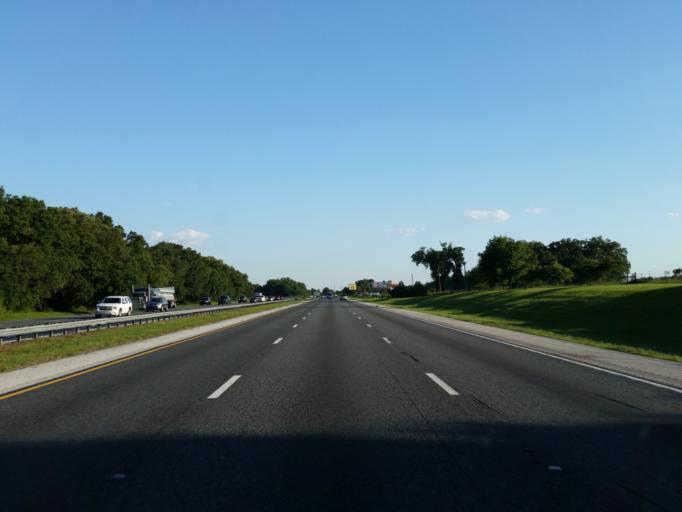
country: US
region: Florida
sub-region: Marion County
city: Ocala
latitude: 29.2405
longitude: -82.1901
